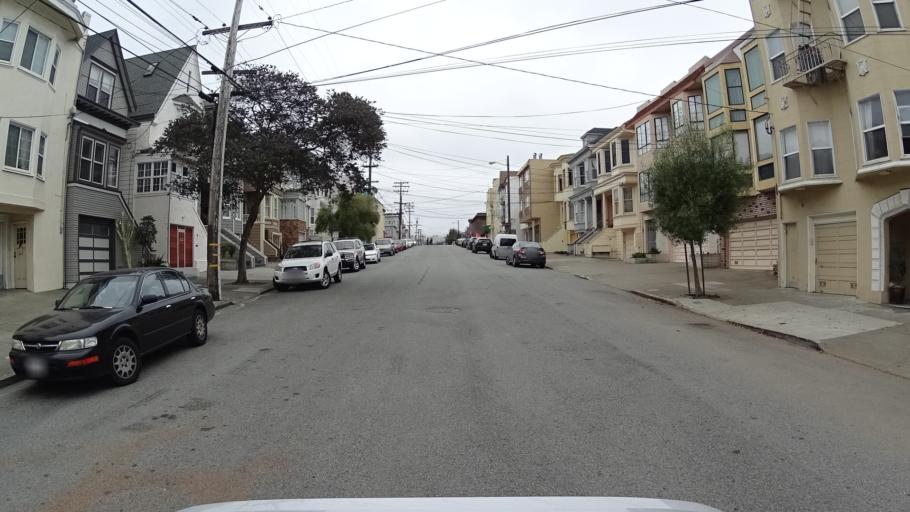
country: US
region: California
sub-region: San Francisco County
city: San Francisco
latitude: 37.7838
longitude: -122.4698
